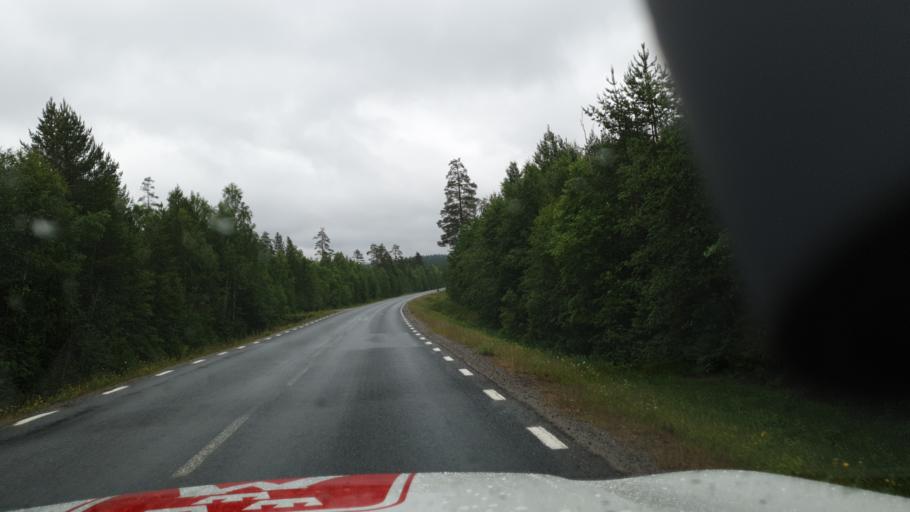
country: SE
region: Vaesterbotten
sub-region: Vannas Kommun
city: Vaennaes
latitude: 63.7820
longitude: 19.7389
